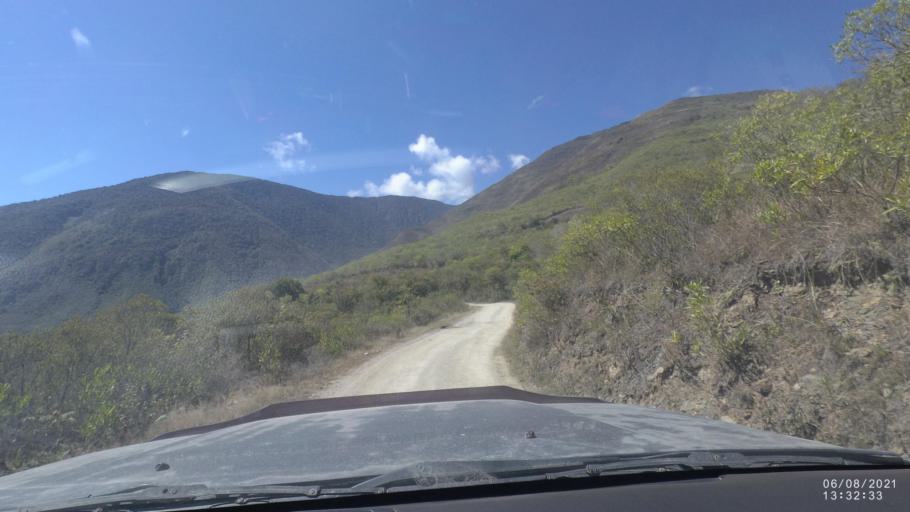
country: BO
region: La Paz
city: Quime
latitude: -16.6986
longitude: -66.7271
